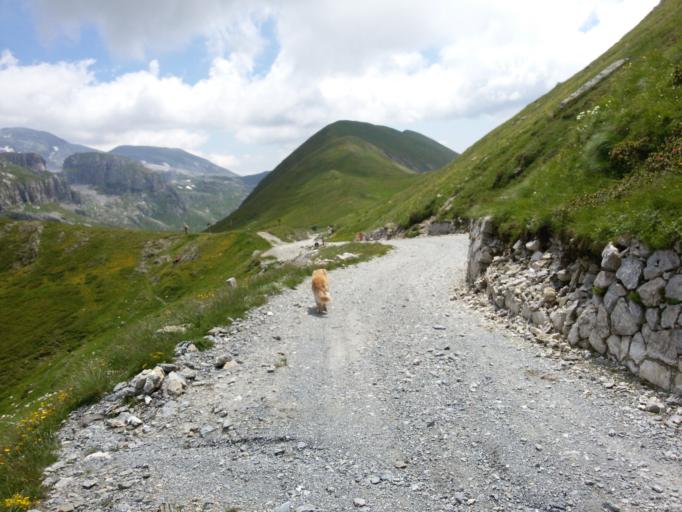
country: IT
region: Piedmont
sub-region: Provincia di Cuneo
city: Limone Piemonte
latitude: 44.1642
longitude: 7.6274
